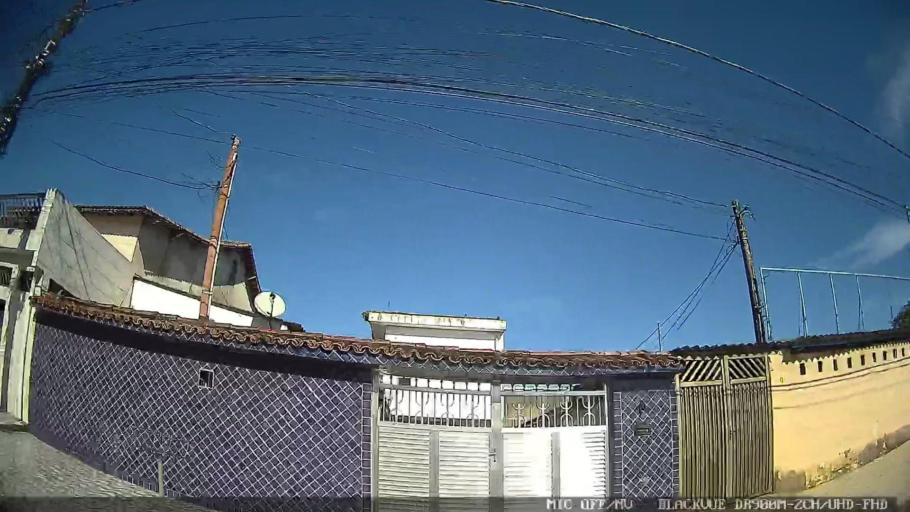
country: BR
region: Sao Paulo
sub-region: Santos
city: Santos
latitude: -23.9377
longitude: -46.2871
